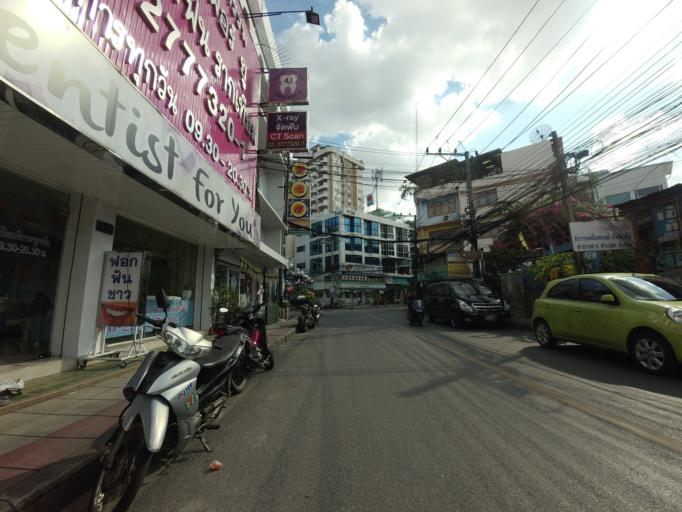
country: TH
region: Bangkok
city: Huai Khwang
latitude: 13.7773
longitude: 100.5832
